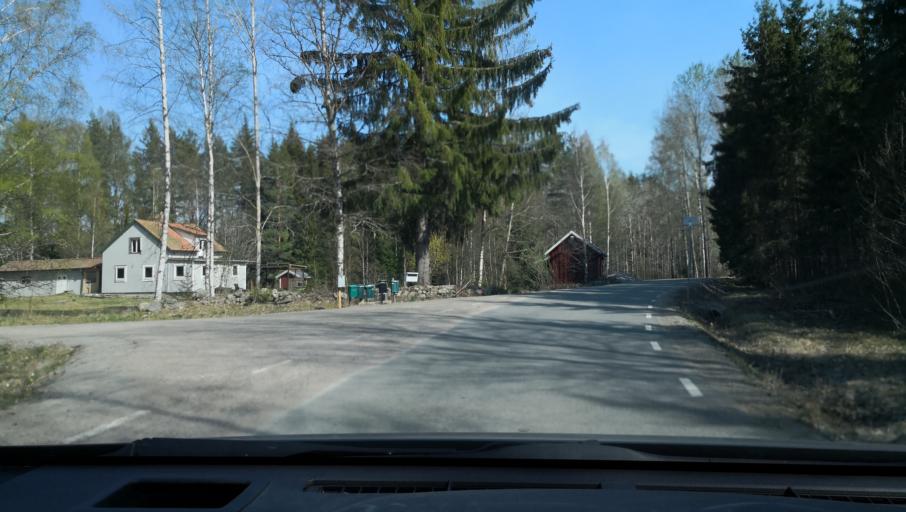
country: SE
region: Vaestmanland
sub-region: Sala Kommun
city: Sala
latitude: 60.0102
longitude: 16.6798
